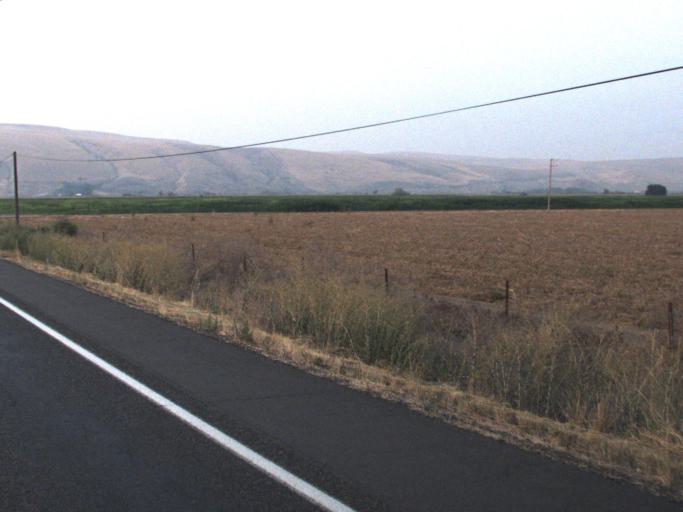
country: US
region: Washington
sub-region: Yakima County
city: Toppenish
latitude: 46.3291
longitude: -120.3205
